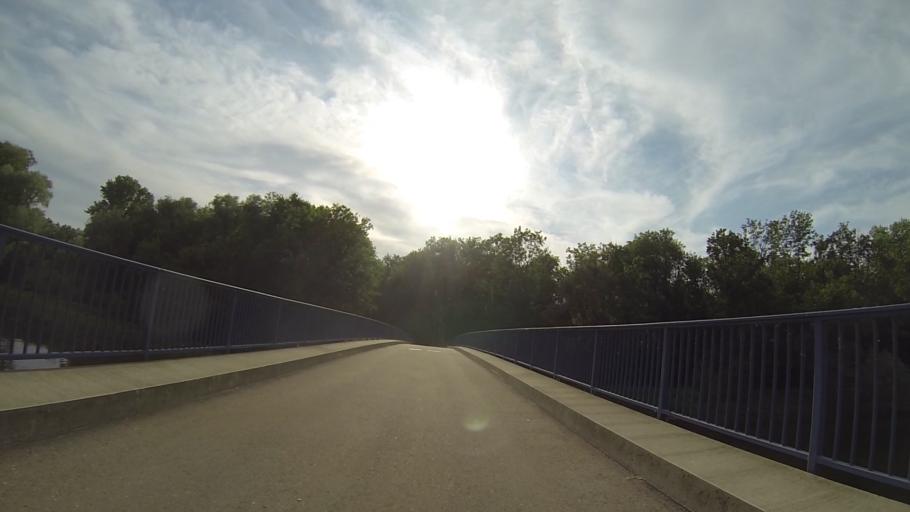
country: DE
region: Baden-Wuerttemberg
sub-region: Tuebingen Region
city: Ulm
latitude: 48.3751
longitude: 9.9640
